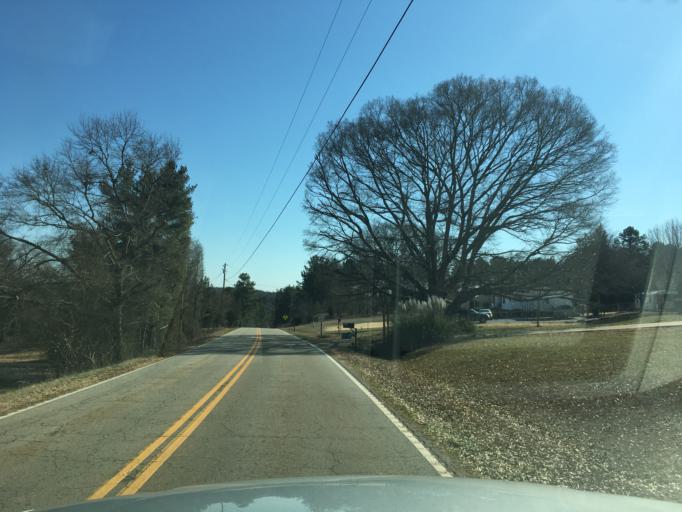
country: US
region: South Carolina
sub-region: Pickens County
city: Liberty
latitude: 34.7980
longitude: -82.7385
